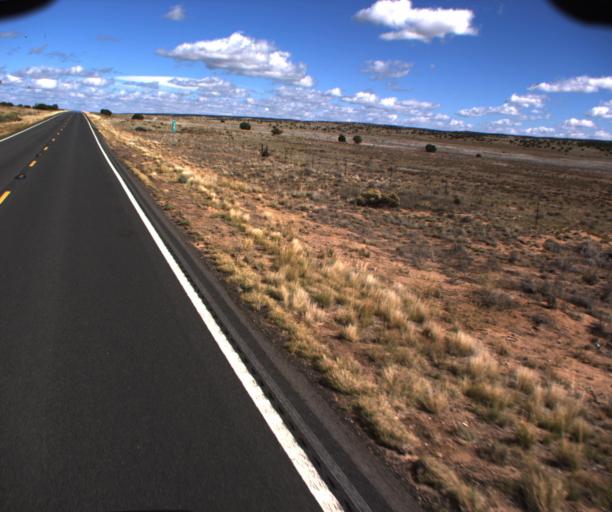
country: US
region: Arizona
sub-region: Apache County
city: Houck
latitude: 34.9357
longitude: -109.2361
